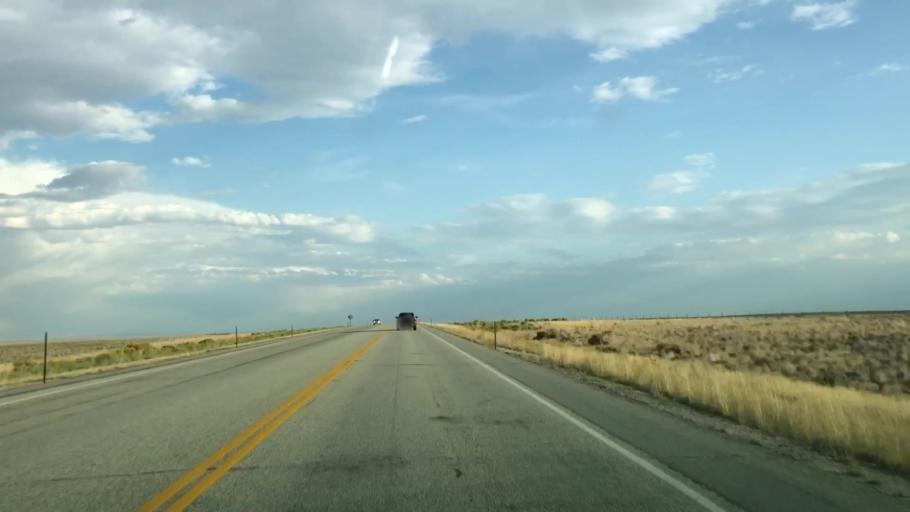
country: US
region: Wyoming
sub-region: Sublette County
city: Marbleton
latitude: 42.3209
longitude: -109.5089
